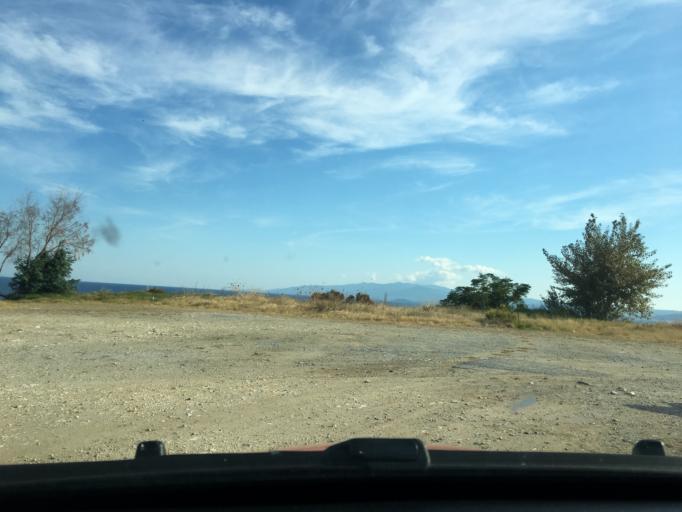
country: GR
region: Central Macedonia
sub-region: Nomos Chalkidikis
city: Agios Nikolaos
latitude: 40.3277
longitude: 23.7062
